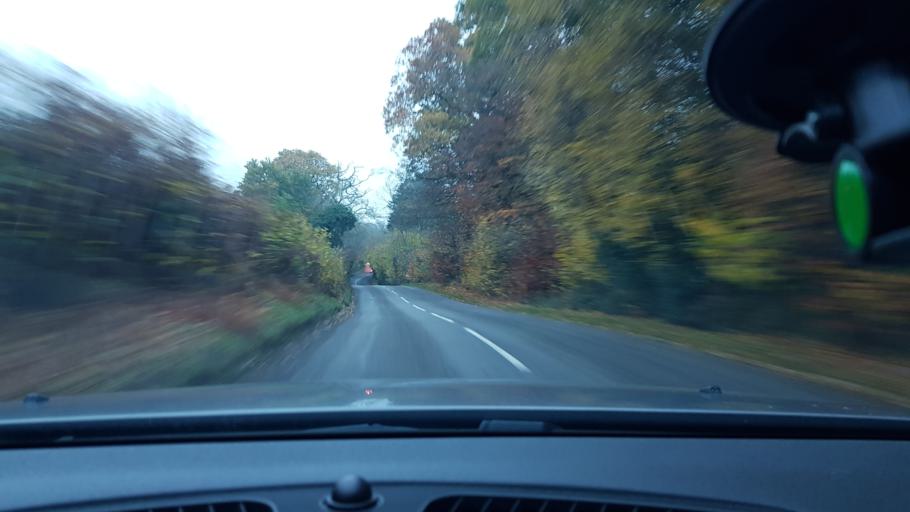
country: GB
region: England
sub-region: Dorset
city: Bovington Camp
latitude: 50.7341
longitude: -2.2772
